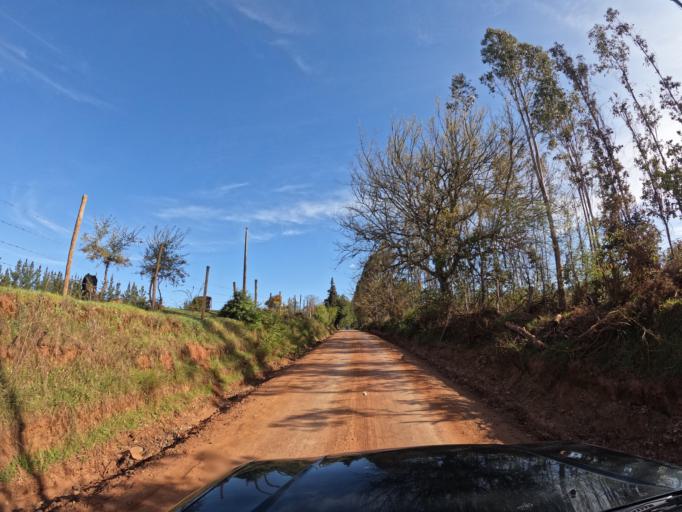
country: CL
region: Biobio
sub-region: Provincia de Biobio
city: La Laja
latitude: -37.1406
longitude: -72.7295
